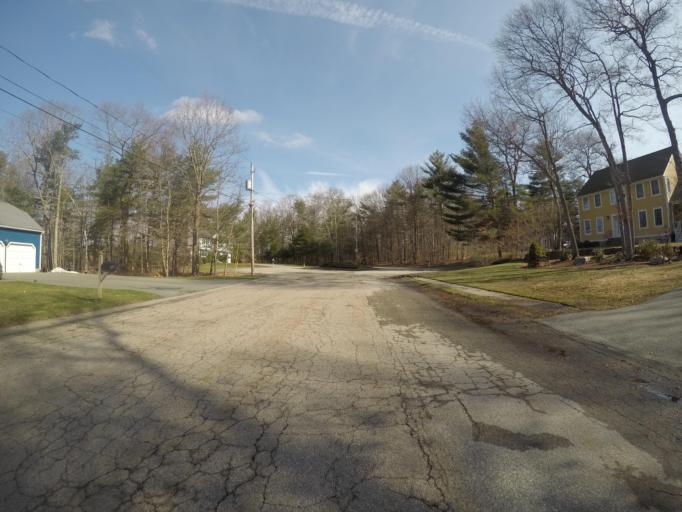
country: US
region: Massachusetts
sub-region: Bristol County
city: Easton
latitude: 42.0220
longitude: -71.1460
